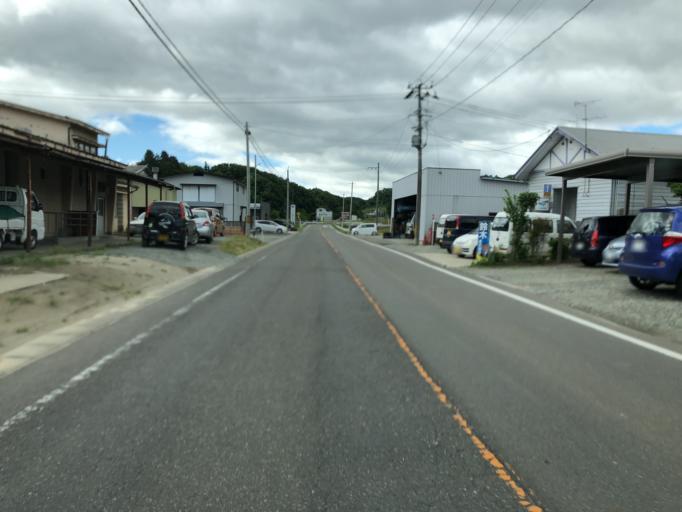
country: JP
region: Fukushima
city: Nihommatsu
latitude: 37.5551
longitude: 140.4597
